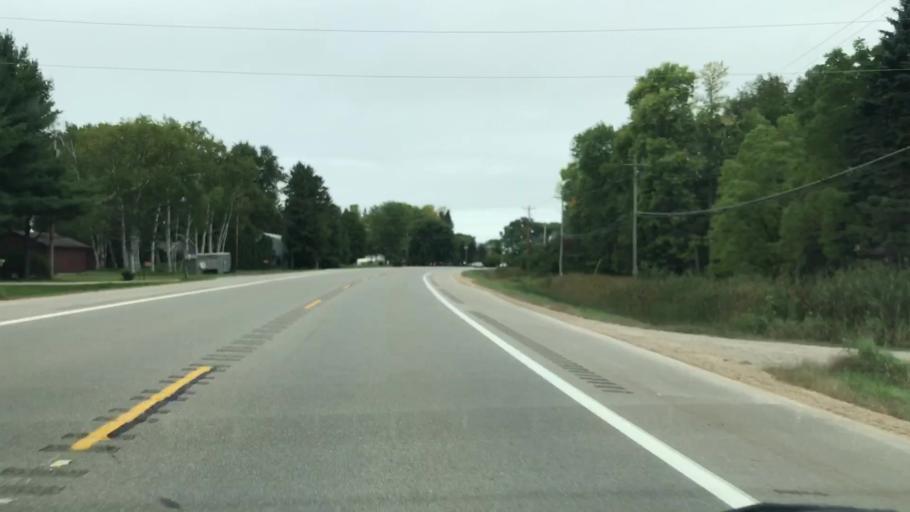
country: US
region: Michigan
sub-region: Menominee County
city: Menominee
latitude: 45.1755
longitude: -87.5714
